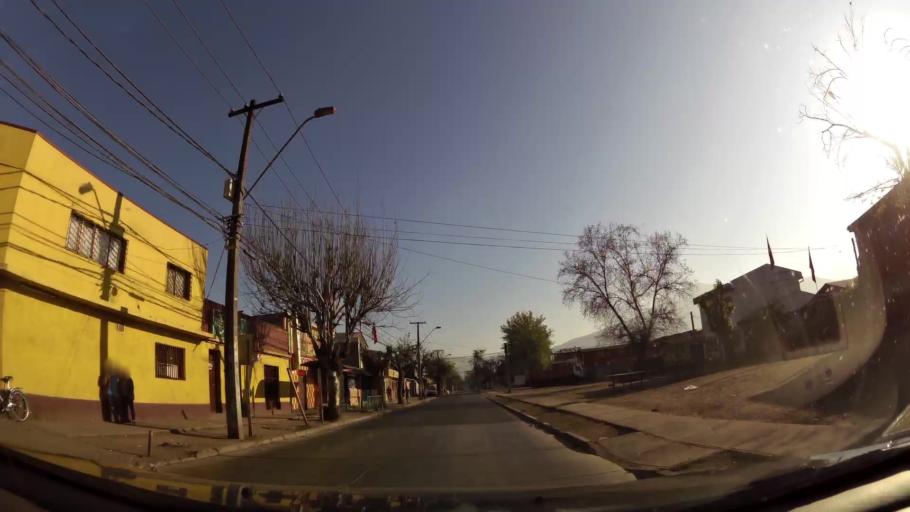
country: CL
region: Santiago Metropolitan
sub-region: Provincia de Santiago
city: Santiago
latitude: -33.3765
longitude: -70.6717
